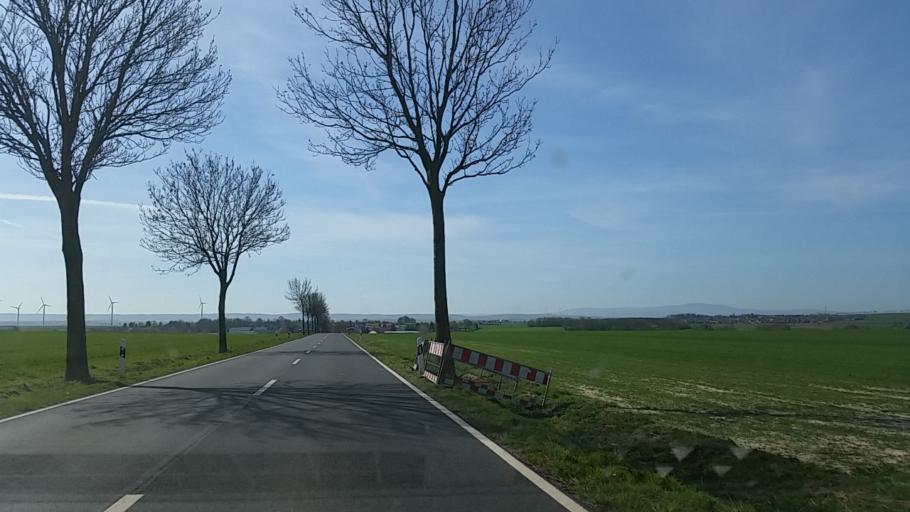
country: DE
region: Lower Saxony
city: Sollingen
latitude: 52.1076
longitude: 10.9274
